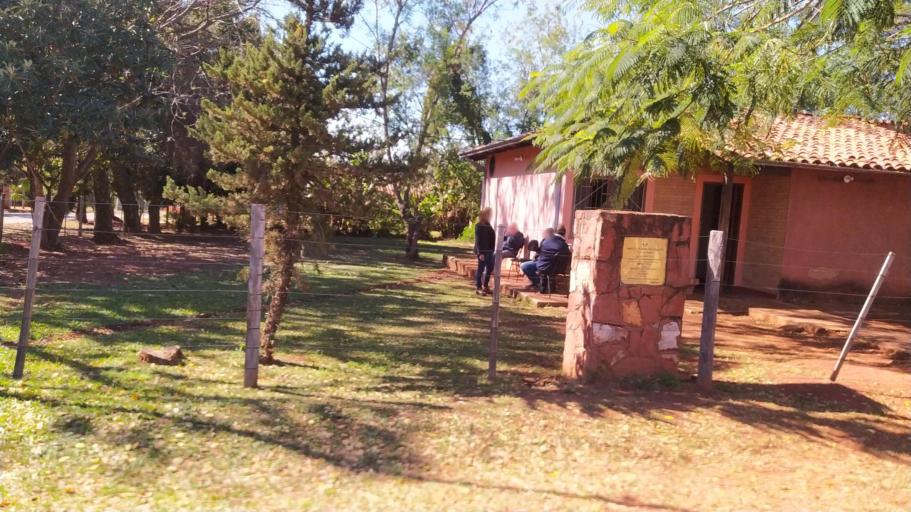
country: PY
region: Misiones
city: San Juan Bautista
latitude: -26.6740
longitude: -57.1384
